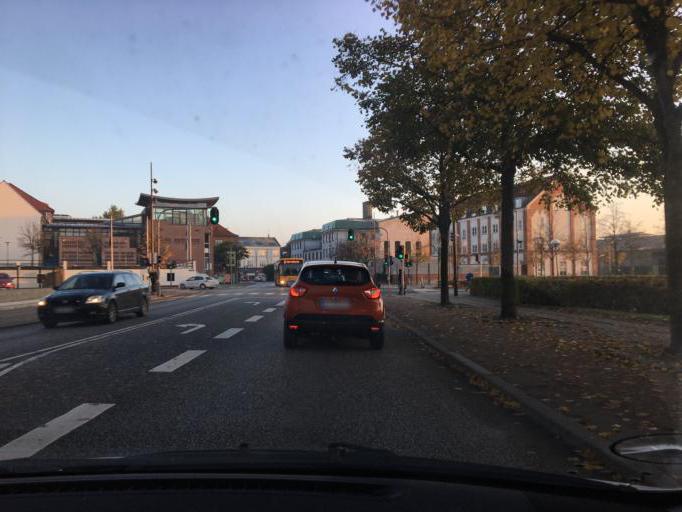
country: DK
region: South Denmark
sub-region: Vejle Kommune
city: Vejle
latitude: 55.7061
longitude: 9.5346
